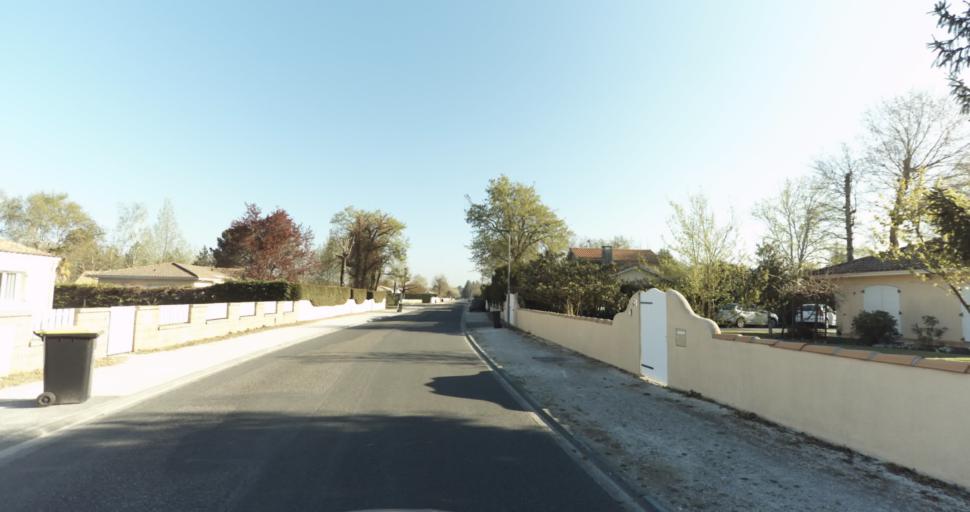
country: FR
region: Aquitaine
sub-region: Departement de la Gironde
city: Martignas-sur-Jalle
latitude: 44.8082
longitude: -0.7942
